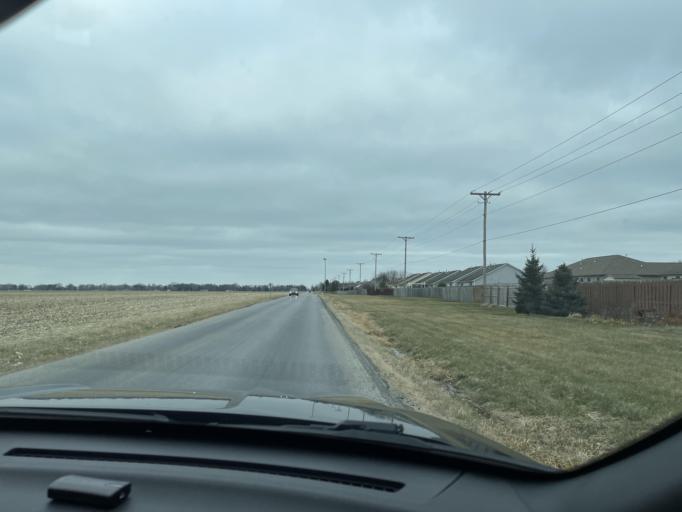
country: US
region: Illinois
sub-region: Sangamon County
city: Jerome
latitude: 39.7714
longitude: -89.7533
